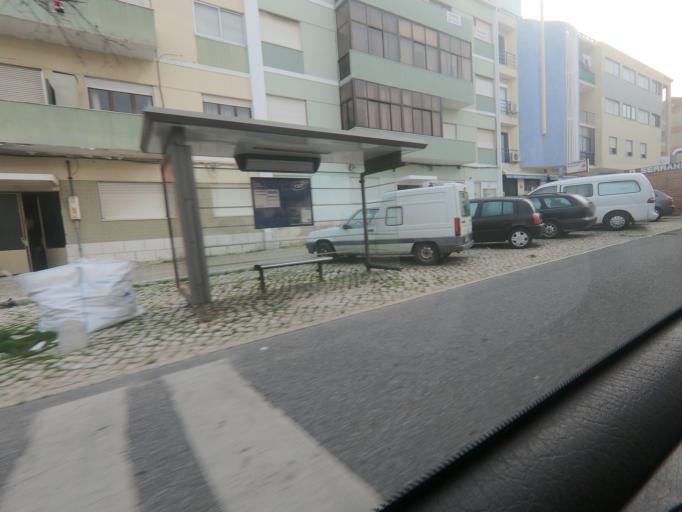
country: PT
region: Setubal
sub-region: Setubal
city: Setubal
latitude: 38.5281
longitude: -8.8753
